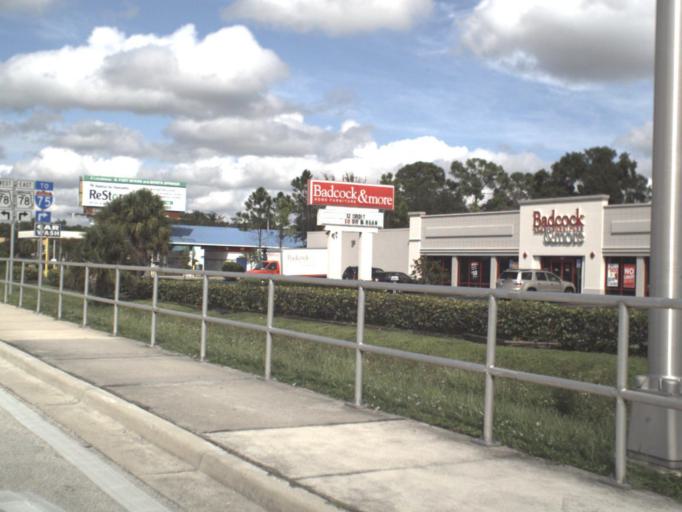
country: US
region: Florida
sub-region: Lee County
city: North Fort Myers
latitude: 26.6803
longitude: -81.8831
